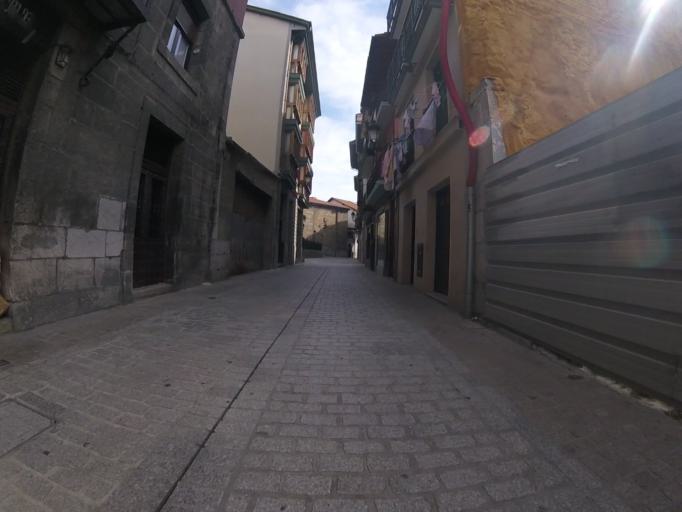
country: ES
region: Basque Country
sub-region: Provincia de Guipuzcoa
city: Azpeitia
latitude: 43.1852
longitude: -2.2648
